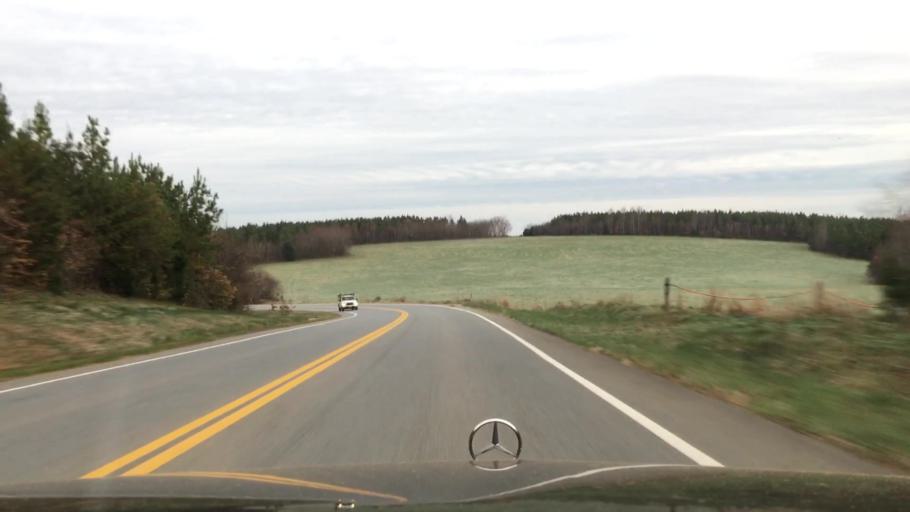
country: US
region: Virginia
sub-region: Campbell County
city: Altavista
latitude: 37.1999
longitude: -79.3006
